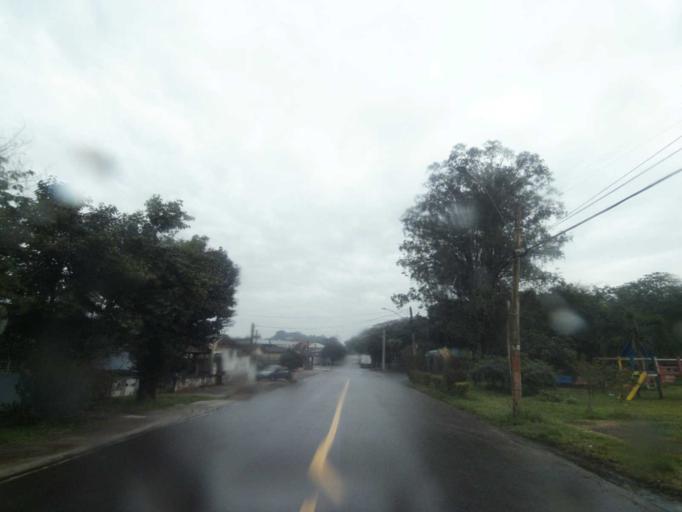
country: BR
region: Rio Grande do Sul
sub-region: Sao Leopoldo
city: Sao Leopoldo
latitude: -29.7888
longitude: -51.1648
